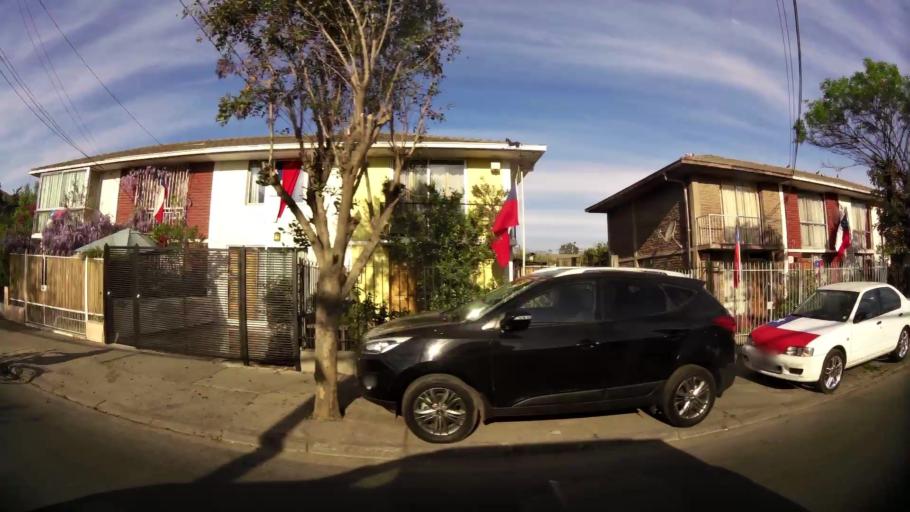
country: CL
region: Santiago Metropolitan
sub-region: Provincia de Santiago
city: Lo Prado
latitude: -33.4705
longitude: -70.6988
